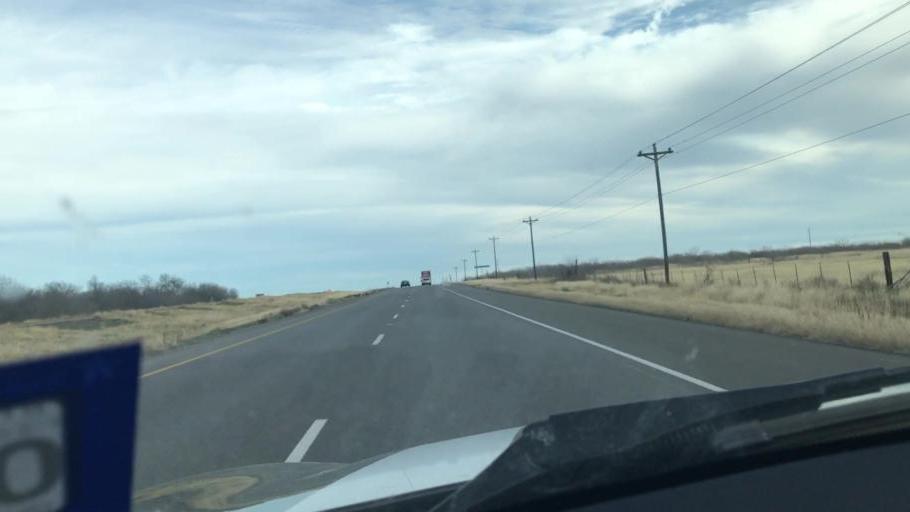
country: US
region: Texas
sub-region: Bastrop County
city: Elgin
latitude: 30.3513
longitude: -97.4538
